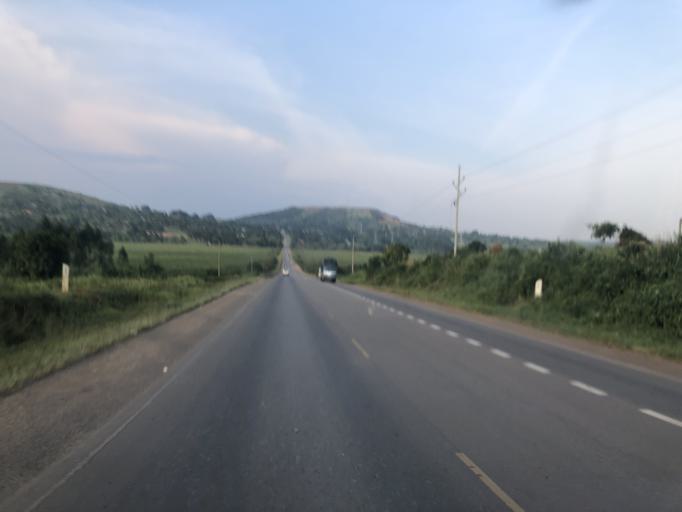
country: UG
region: Central Region
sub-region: Mpigi District
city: Mpigi
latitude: 0.1812
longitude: 32.2818
